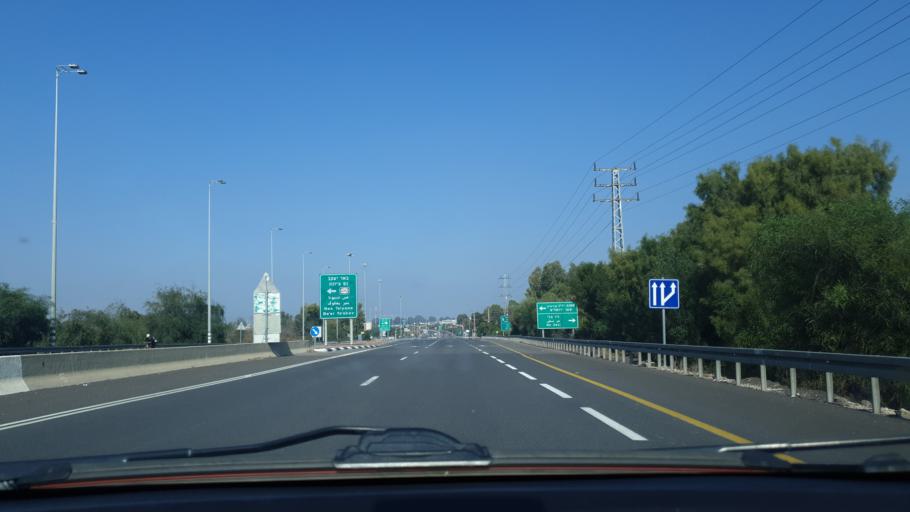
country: IL
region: Central District
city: Ramla
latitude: 31.9485
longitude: 34.8582
